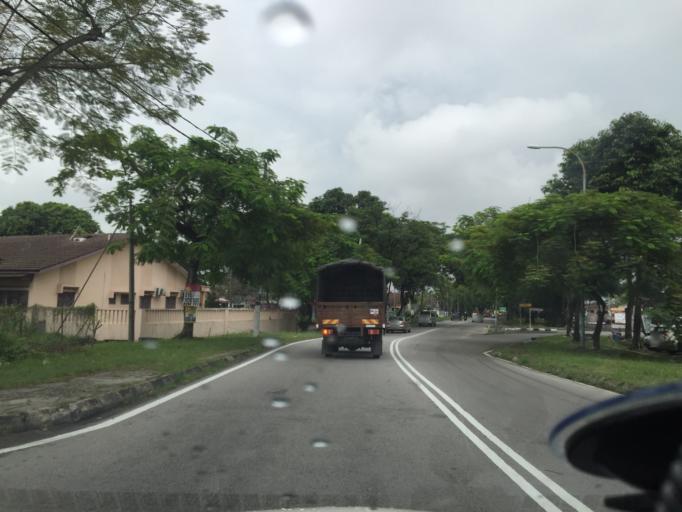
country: MY
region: Selangor
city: Klang
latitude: 3.0096
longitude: 101.4422
